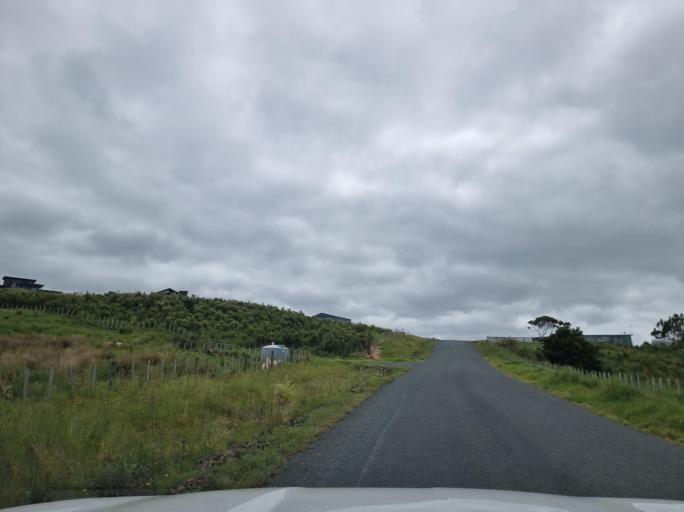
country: NZ
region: Auckland
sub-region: Auckland
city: Wellsford
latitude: -36.1737
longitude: 174.5580
